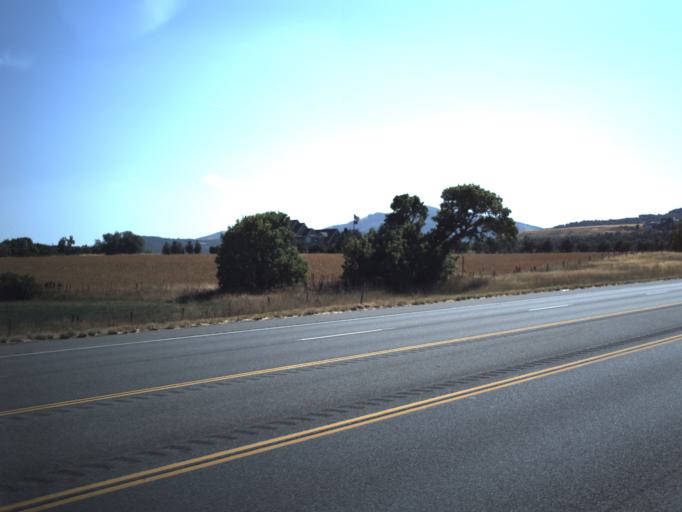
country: US
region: Utah
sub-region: Cache County
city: Wellsville
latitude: 41.6132
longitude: -111.9360
